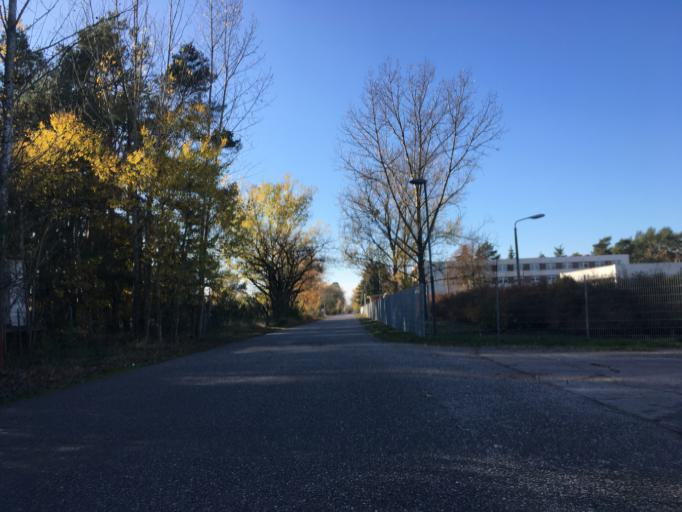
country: DE
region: Brandenburg
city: Spreenhagen
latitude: 52.3409
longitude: 13.8965
